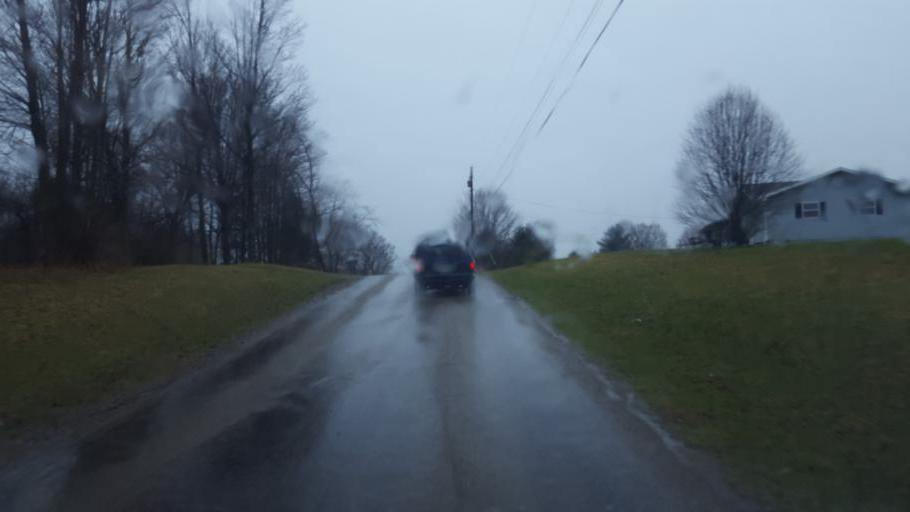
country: US
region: Ohio
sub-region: Knox County
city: Mount Vernon
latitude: 40.4205
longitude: -82.4830
